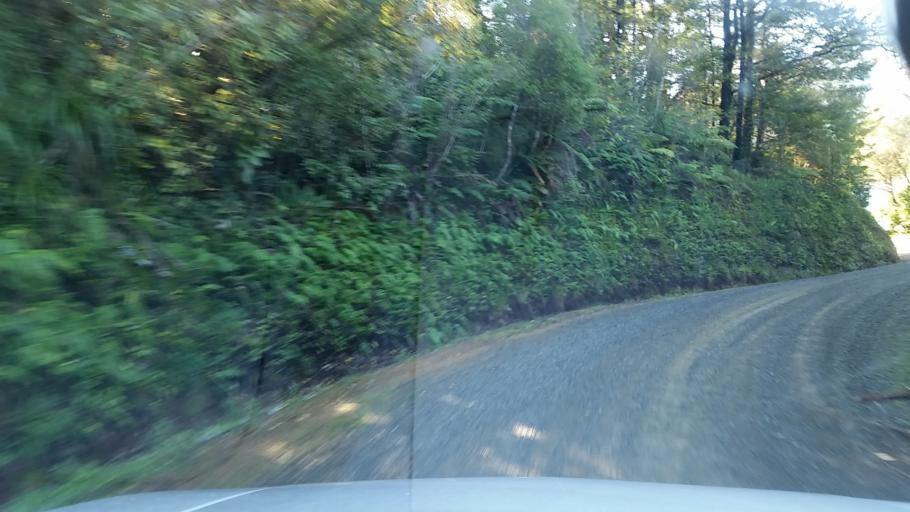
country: NZ
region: Marlborough
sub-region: Marlborough District
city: Picton
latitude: -41.1056
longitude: 173.6539
